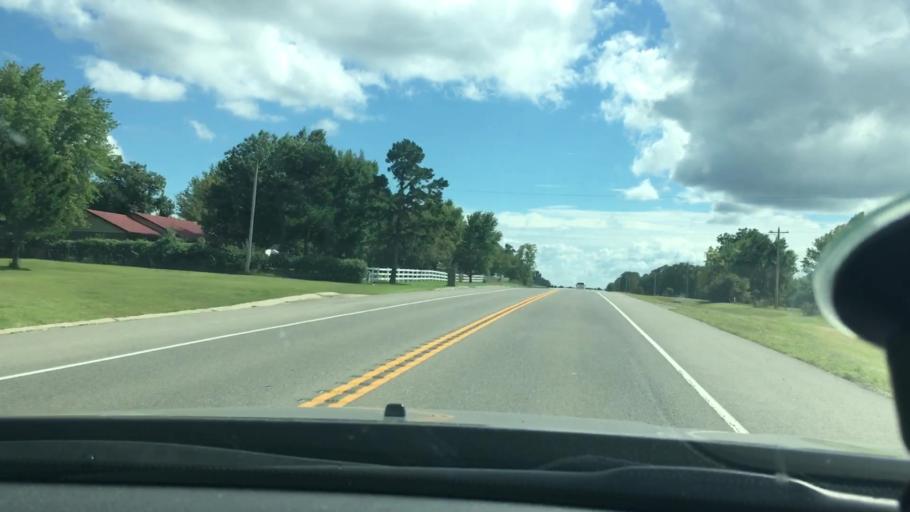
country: US
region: Oklahoma
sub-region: Sequoyah County
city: Vian
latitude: 35.6056
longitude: -94.9763
